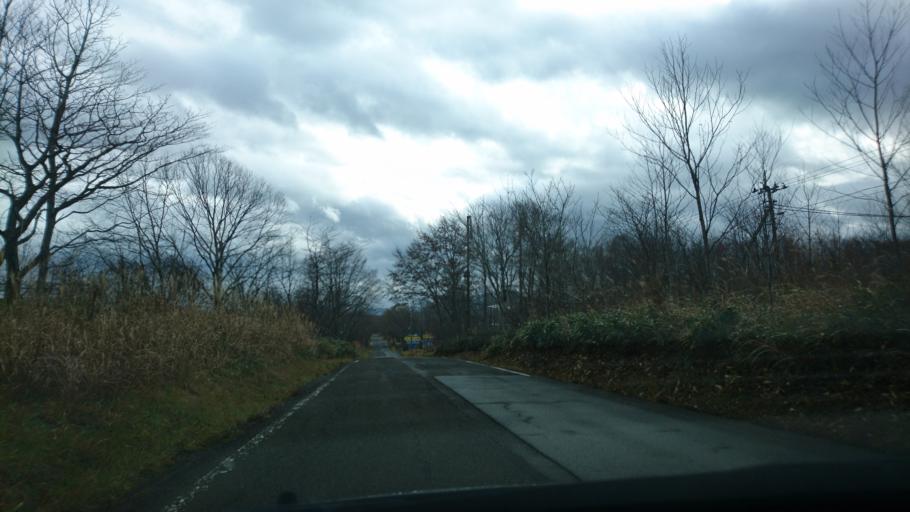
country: JP
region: Iwate
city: Ichinoseki
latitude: 38.9370
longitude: 140.8319
